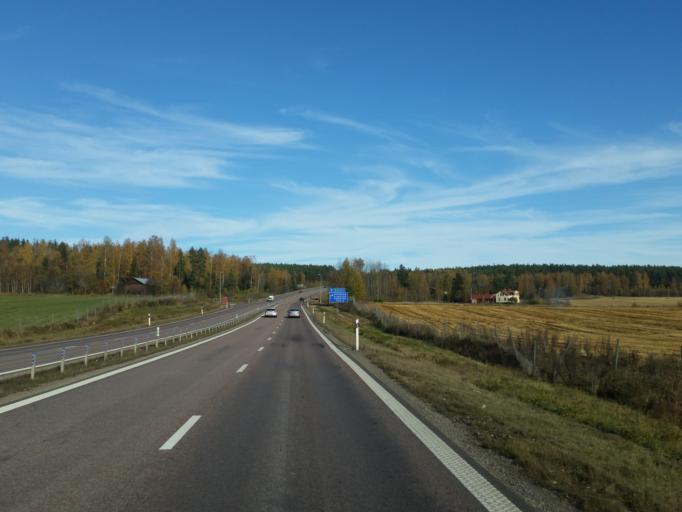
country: SE
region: Dalarna
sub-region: Borlange Kommun
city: Ornas
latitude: 60.5447
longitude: 15.5657
